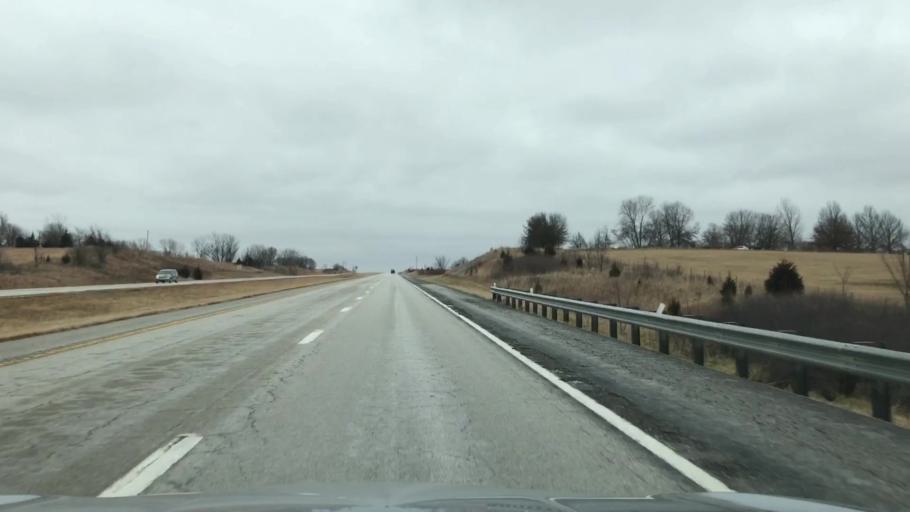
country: US
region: Missouri
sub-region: Caldwell County
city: Hamilton
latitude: 39.7498
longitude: -94.0962
